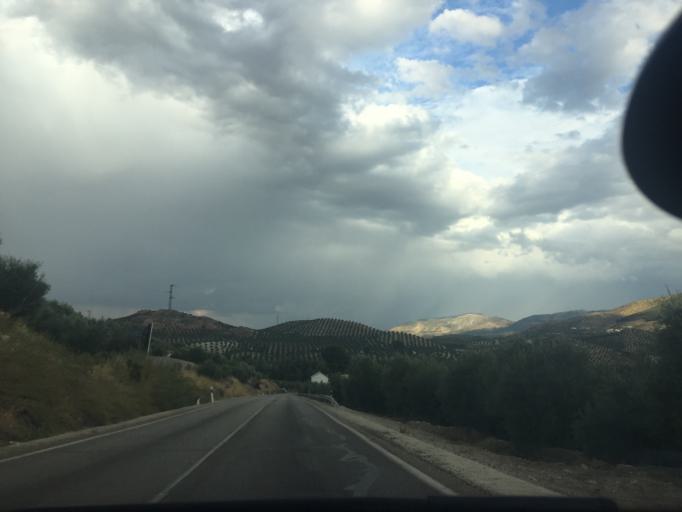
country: ES
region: Andalusia
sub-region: Provincia de Jaen
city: Jaen
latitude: 37.7608
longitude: -3.7619
